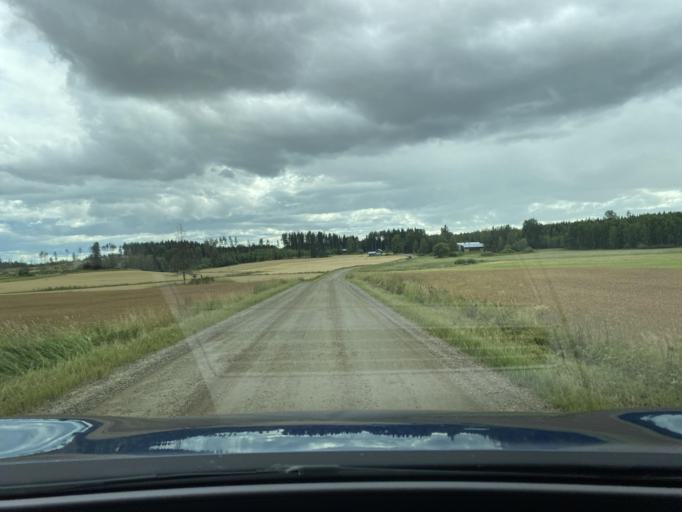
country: FI
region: Pirkanmaa
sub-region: Lounais-Pirkanmaa
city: Punkalaidun
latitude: 61.1843
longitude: 23.1853
